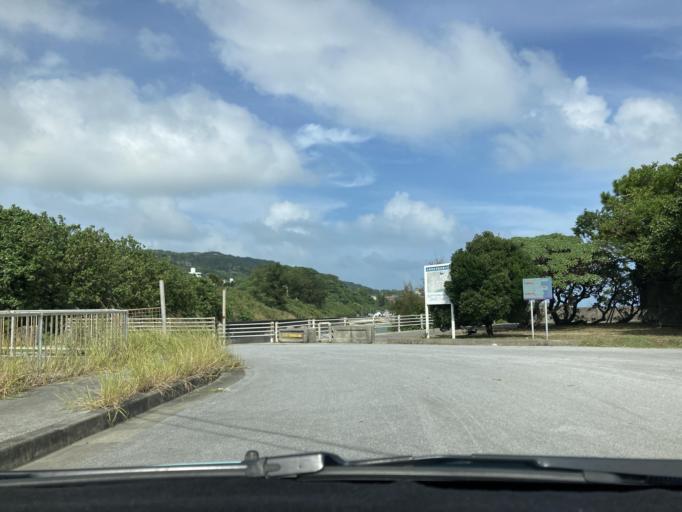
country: JP
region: Okinawa
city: Ginowan
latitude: 26.1513
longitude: 127.8079
